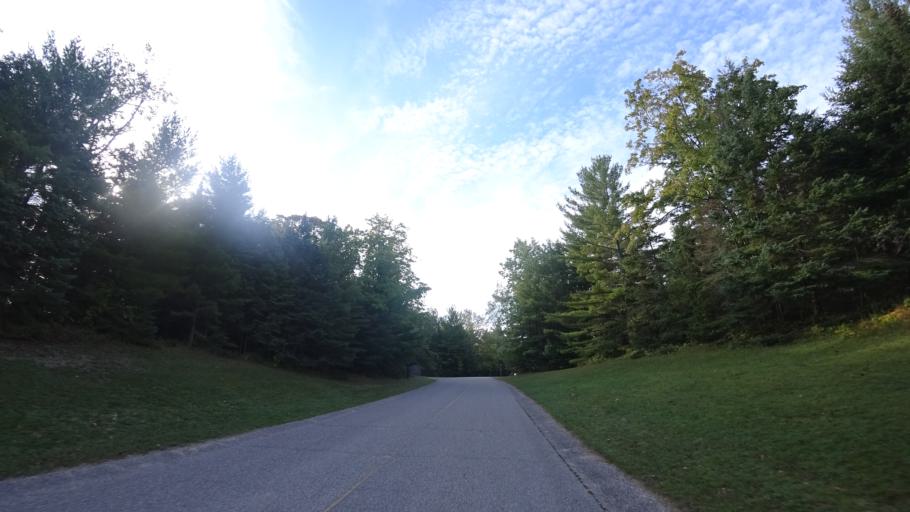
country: US
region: Michigan
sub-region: Mackinac County
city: Saint Ignace
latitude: 45.7452
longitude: -84.8995
